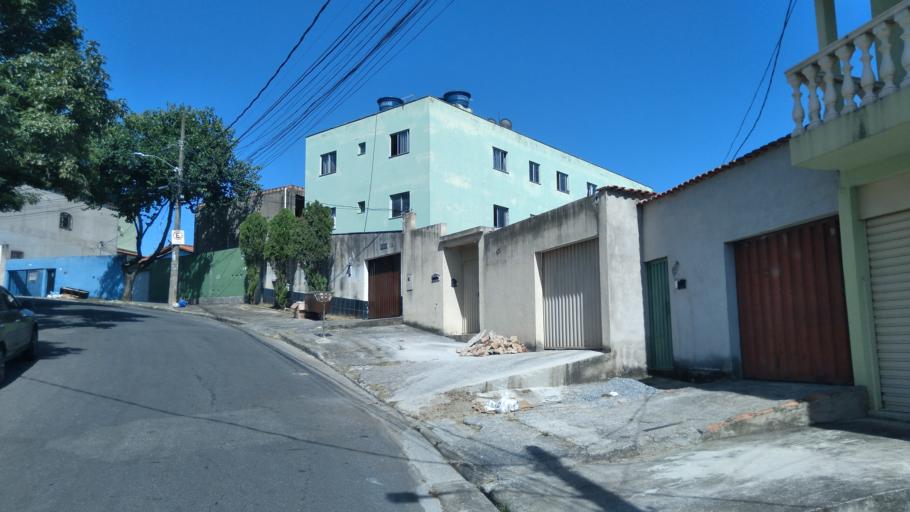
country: BR
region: Minas Gerais
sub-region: Belo Horizonte
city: Belo Horizonte
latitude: -19.8451
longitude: -43.9049
